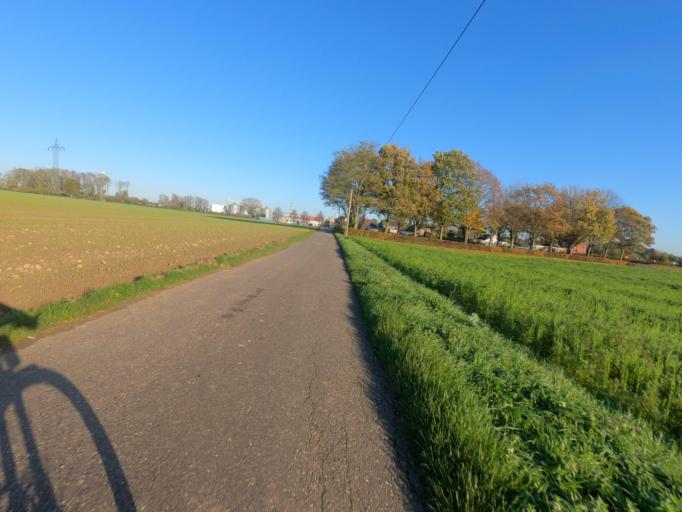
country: DE
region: North Rhine-Westphalia
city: Erkelenz
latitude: 51.0783
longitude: 6.3410
